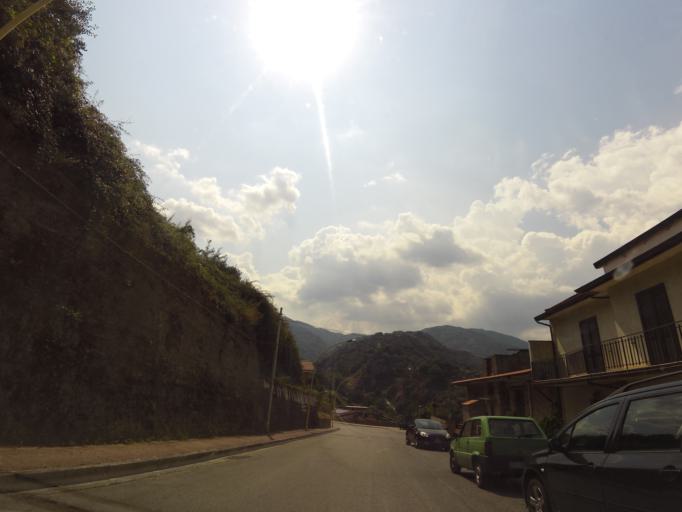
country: IT
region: Calabria
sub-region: Provincia di Reggio Calabria
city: Bivongi
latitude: 38.4814
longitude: 16.4514
